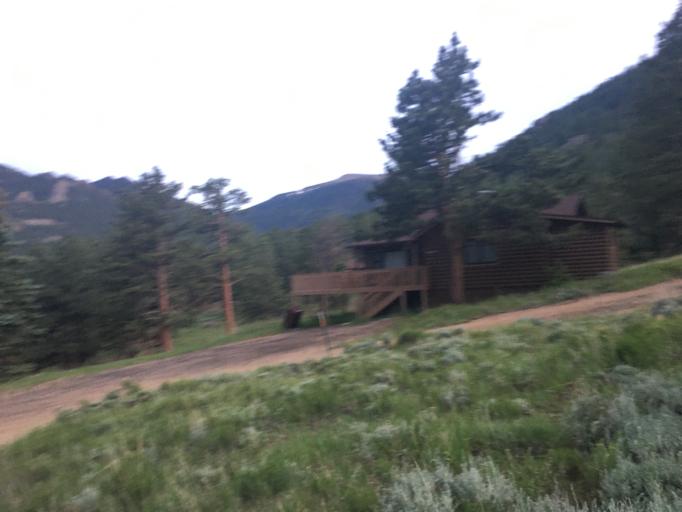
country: US
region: Colorado
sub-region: Larimer County
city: Estes Park
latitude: 40.3370
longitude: -105.5797
